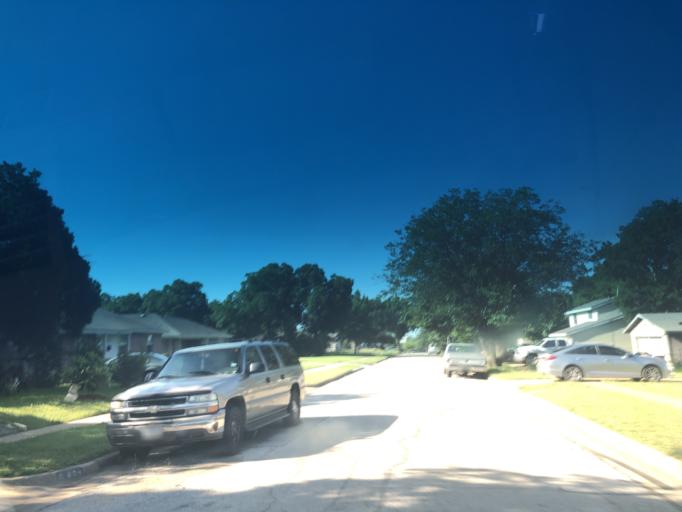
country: US
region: Texas
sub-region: Dallas County
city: Grand Prairie
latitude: 32.7320
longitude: -97.0385
